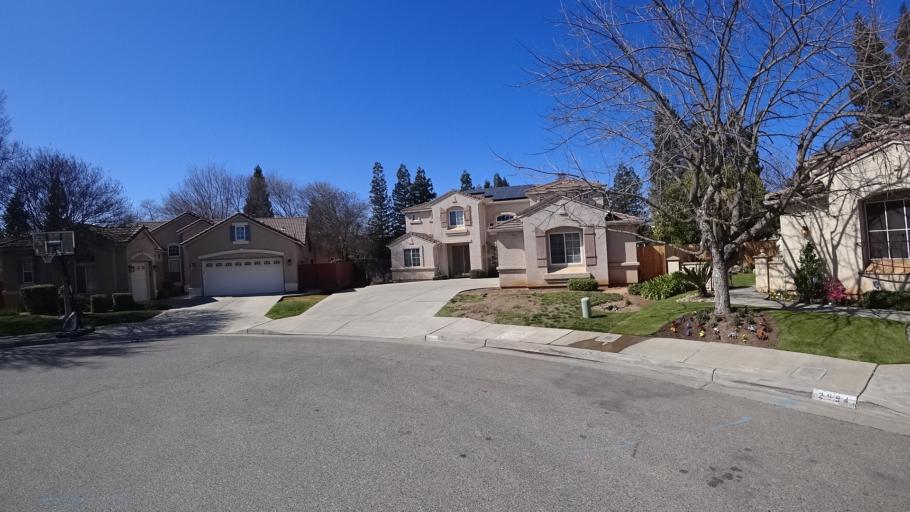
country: US
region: California
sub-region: Fresno County
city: Clovis
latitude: 36.8773
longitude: -119.7372
